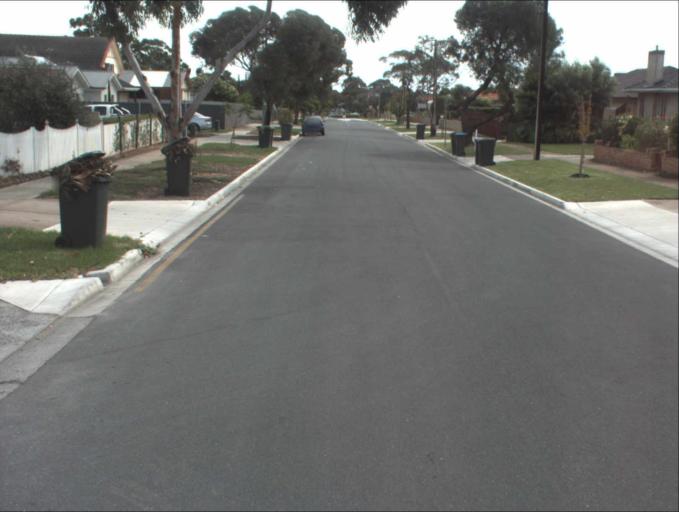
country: AU
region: South Australia
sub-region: Port Adelaide Enfield
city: Enfield
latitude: -34.8651
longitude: 138.6178
